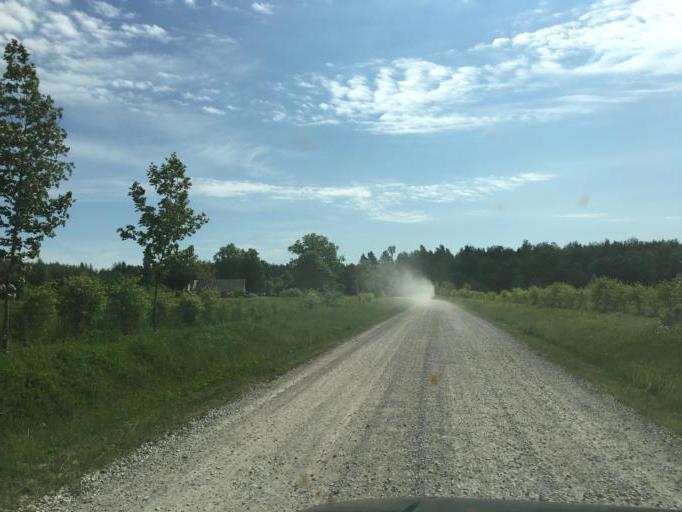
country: LV
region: Talsu Rajons
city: Valdemarpils
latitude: 57.3724
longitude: 22.5216
